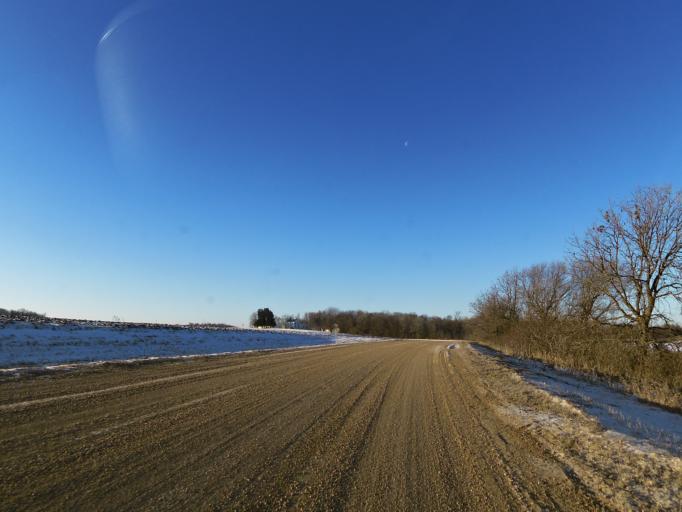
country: US
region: Minnesota
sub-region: Scott County
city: Jordan
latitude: 44.6738
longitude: -93.5390
